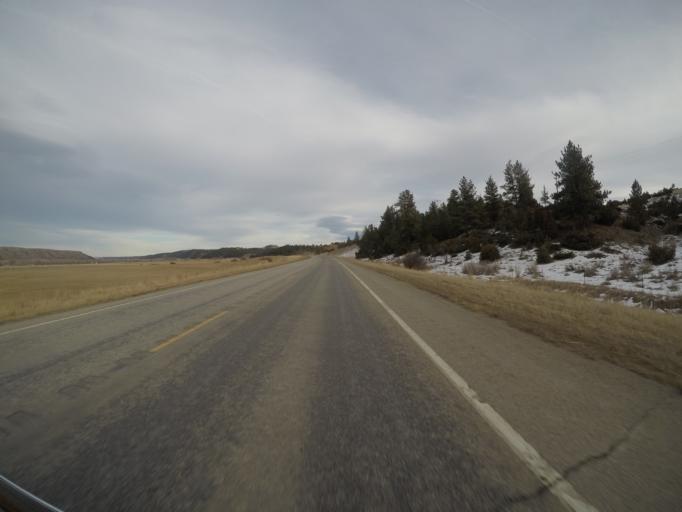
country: US
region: Montana
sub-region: Stillwater County
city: Absarokee
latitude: 45.5436
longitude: -109.3897
